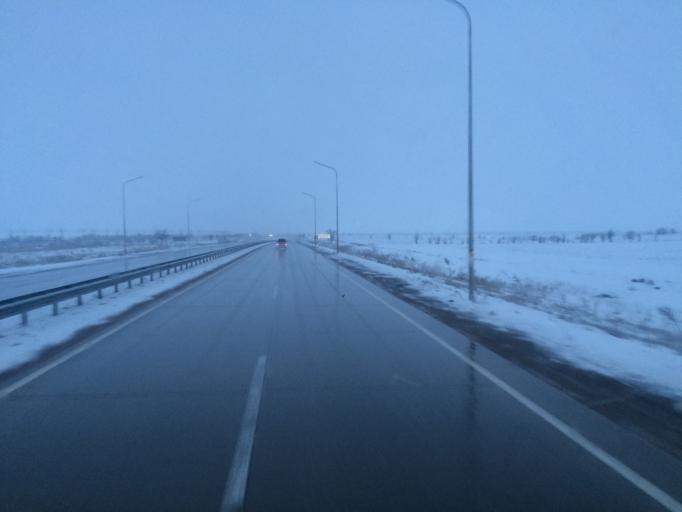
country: KZ
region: Zhambyl
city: Kulan
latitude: 42.9931
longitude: 72.3096
